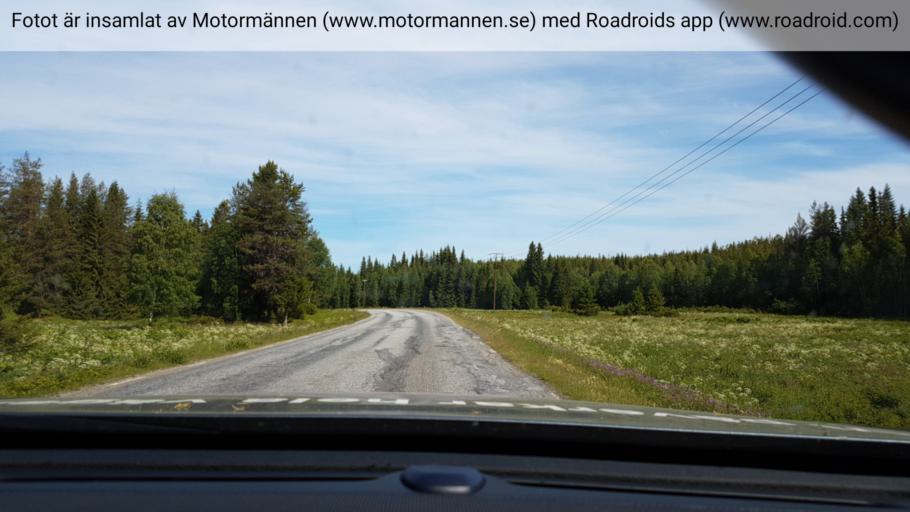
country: SE
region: Vaesterbotten
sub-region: Vilhelmina Kommun
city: Sjoberg
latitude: 64.5089
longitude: 15.9234
